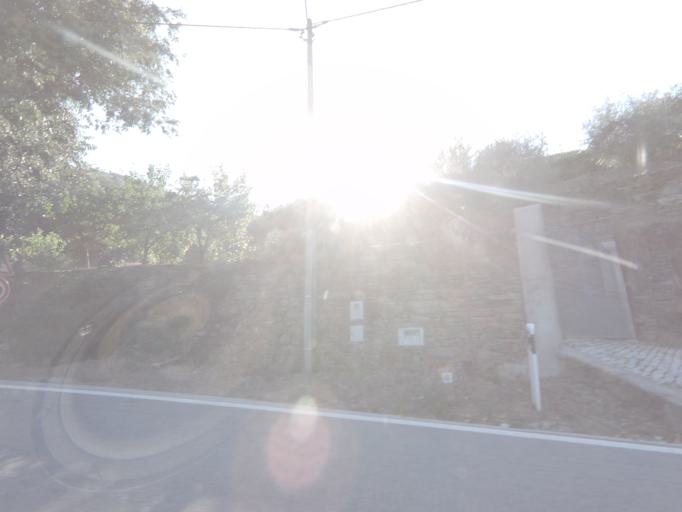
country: PT
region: Viseu
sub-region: Tabuaco
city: Tabuaco
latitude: 41.1420
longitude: -7.5740
